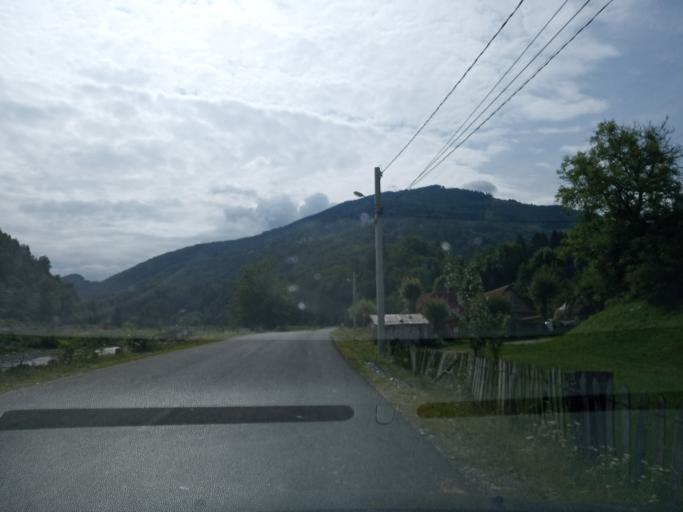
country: RO
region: Hunedoara
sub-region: Oras Petrila
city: Petrila
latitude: 45.4176
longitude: 23.4315
